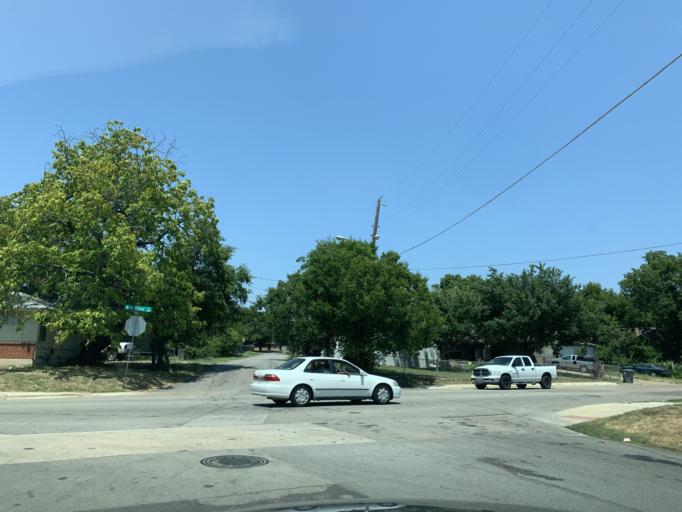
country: US
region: Texas
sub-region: Dallas County
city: Dallas
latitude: 32.6923
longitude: -96.8043
